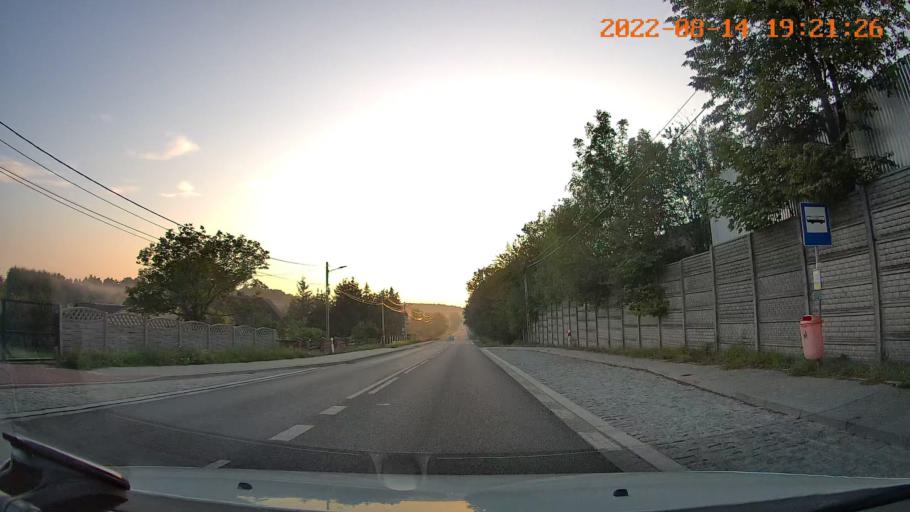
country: PL
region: Swietokrzyskie
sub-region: Powiat kielecki
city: Piekoszow
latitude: 50.8588
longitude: 20.4949
